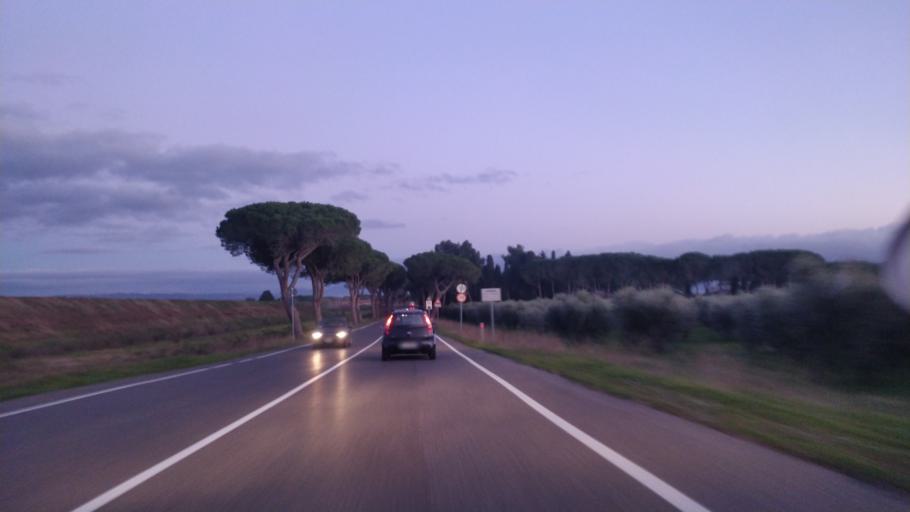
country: IT
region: Tuscany
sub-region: Provincia di Livorno
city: S.P. in Palazzi
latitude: 43.3353
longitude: 10.4903
